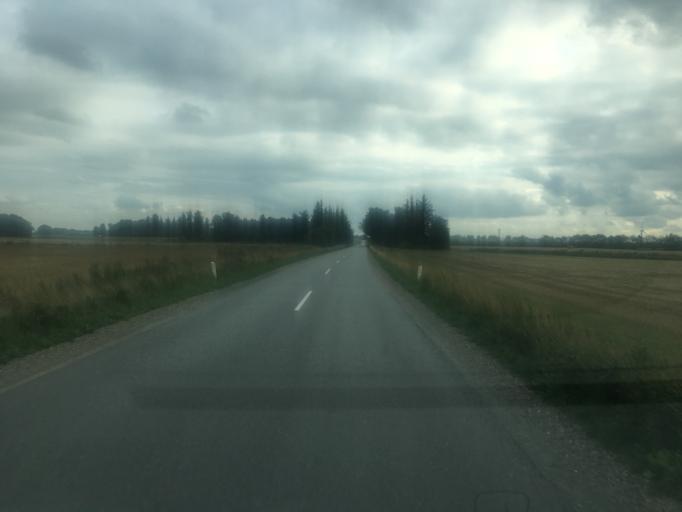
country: DK
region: South Denmark
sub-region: Tonder Kommune
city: Logumkloster
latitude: 54.9871
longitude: 8.9614
